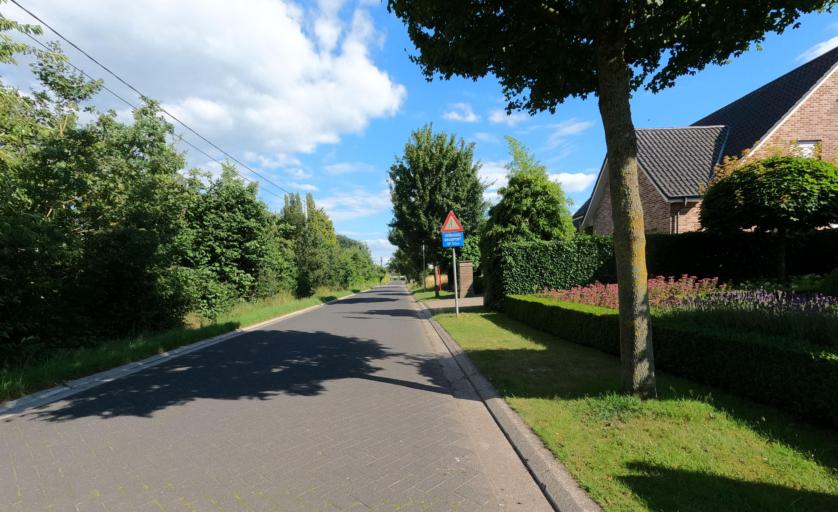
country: BE
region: Flanders
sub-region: Provincie Antwerpen
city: Wuustwezel
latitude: 51.3652
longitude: 4.5577
